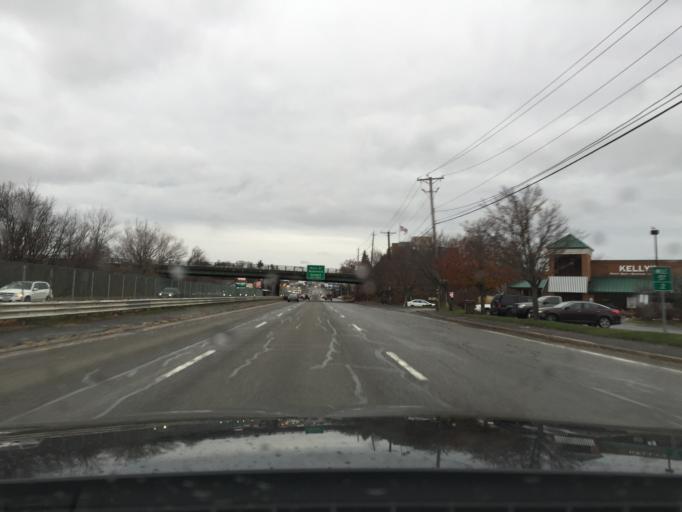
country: US
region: Massachusetts
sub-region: Essex County
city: Saugus
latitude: 42.4815
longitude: -71.0208
